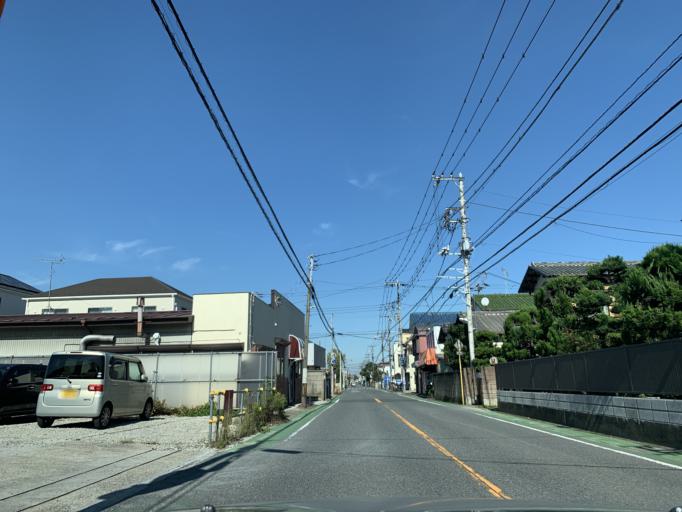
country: JP
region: Tokyo
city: Urayasu
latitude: 35.6970
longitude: 139.9201
